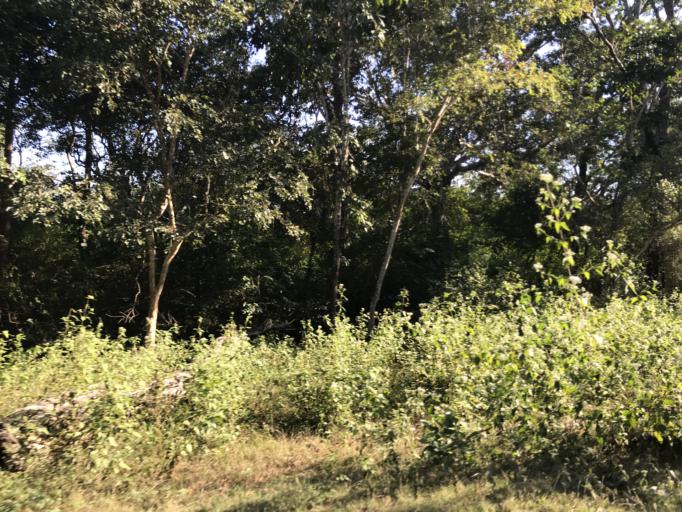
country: IN
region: Karnataka
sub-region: Mysore
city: Heggadadevankote
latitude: 11.9636
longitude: 76.2422
